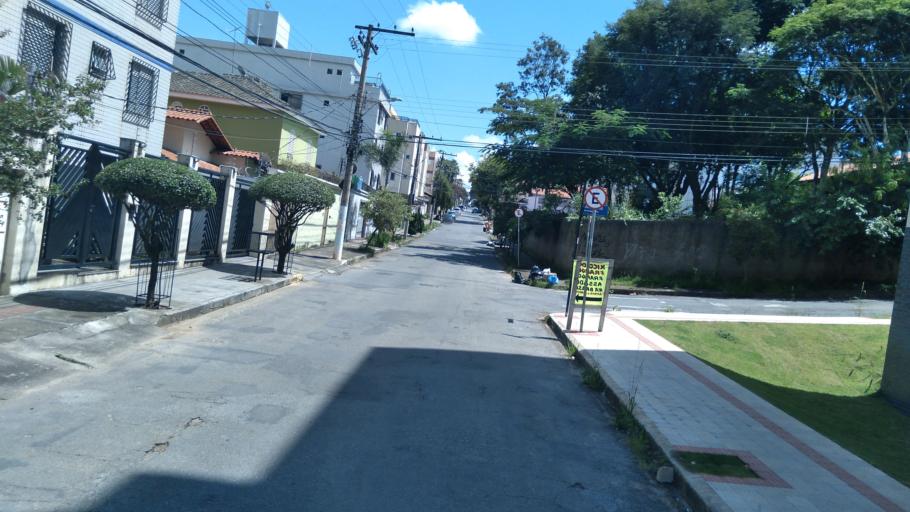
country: BR
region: Minas Gerais
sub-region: Belo Horizonte
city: Belo Horizonte
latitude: -19.8719
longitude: -43.9211
